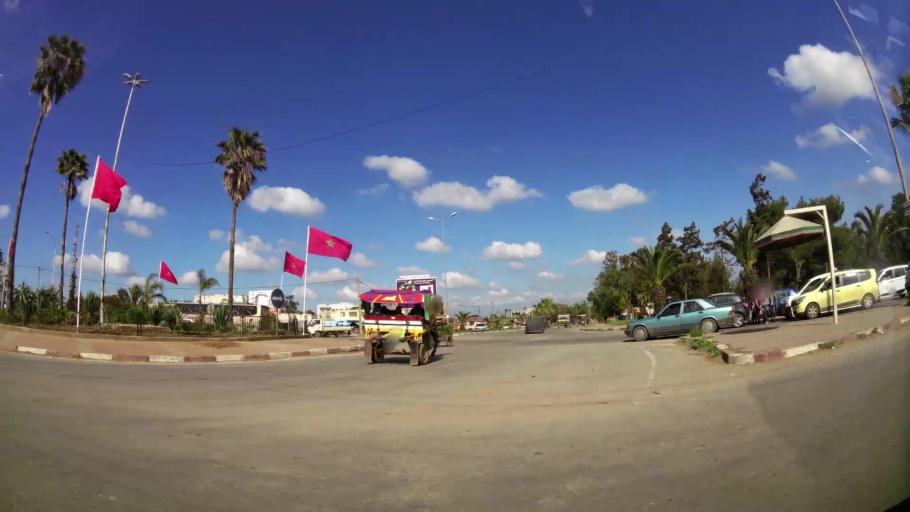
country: MA
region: Grand Casablanca
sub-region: Mediouna
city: Mediouna
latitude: 33.4526
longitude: -7.5217
